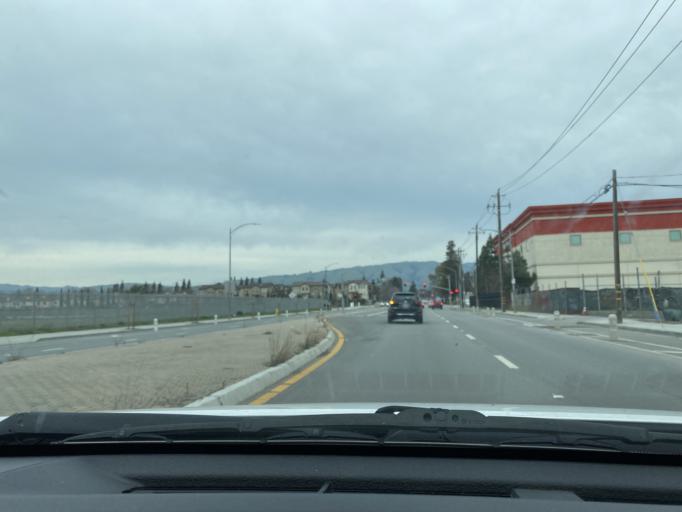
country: US
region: California
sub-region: Santa Clara County
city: San Jose
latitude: 37.3644
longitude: -121.8730
